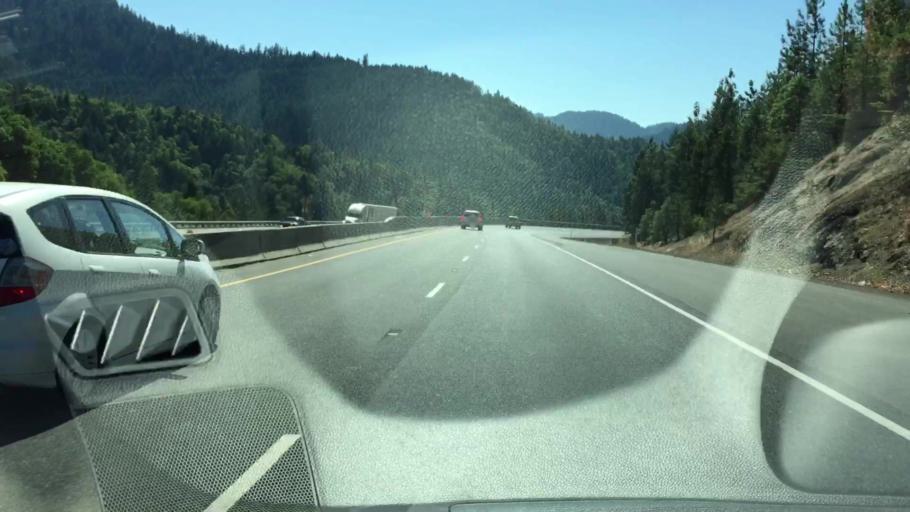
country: US
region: Oregon
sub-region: Josephine County
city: Merlin
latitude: 42.6581
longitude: -123.3770
